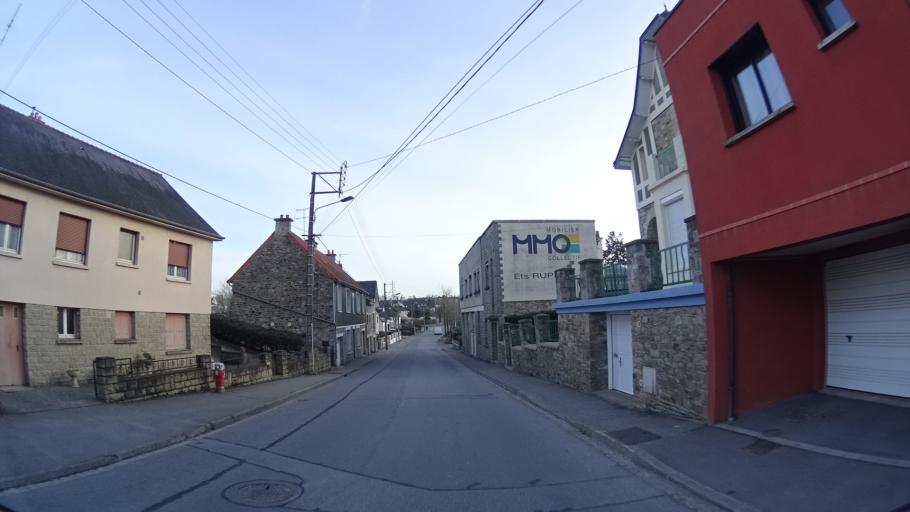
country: FR
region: Brittany
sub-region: Departement d'Ille-et-Vilaine
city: Vitre
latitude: 48.1193
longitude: -1.2169
